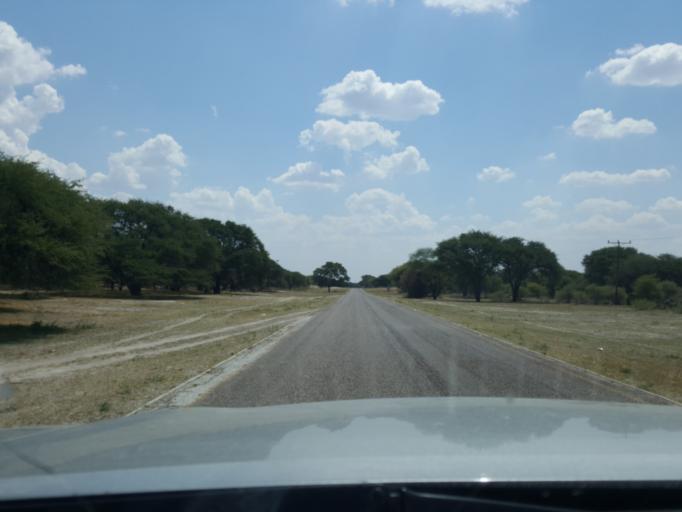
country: BW
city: Tsau
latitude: -20.1831
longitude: 22.4680
